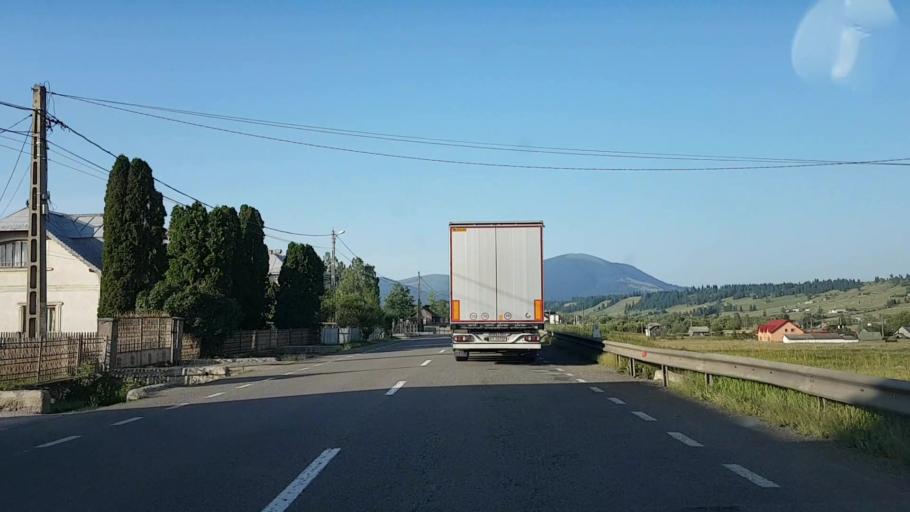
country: RO
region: Suceava
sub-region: Comuna Poiana Stampei
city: Poiana Stampei
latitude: 47.3311
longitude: 25.1550
